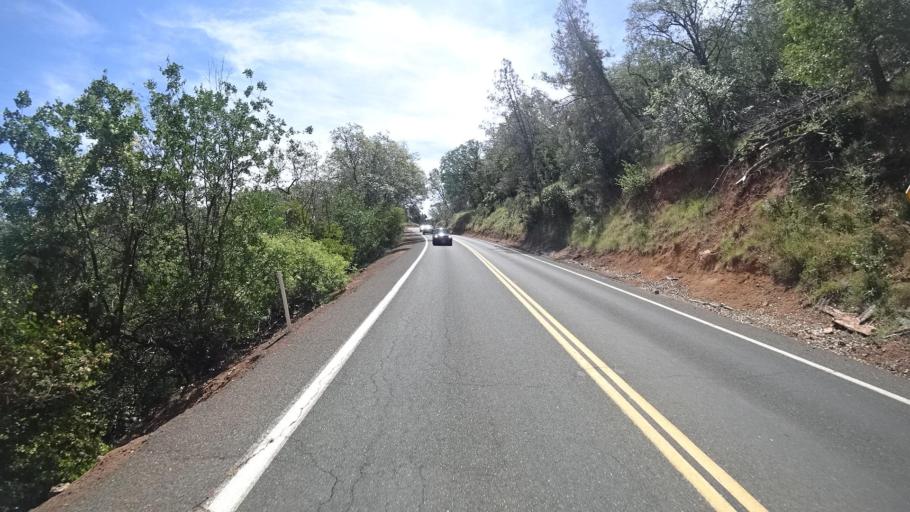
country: US
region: California
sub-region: Lake County
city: Clearlake
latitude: 38.9420
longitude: -122.6704
